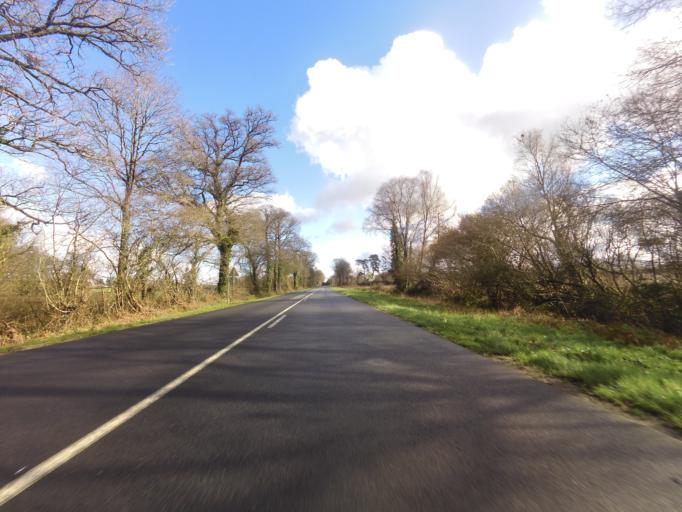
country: FR
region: Brittany
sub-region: Departement du Morbihan
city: Guemene-sur-Scorff
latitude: 48.0607
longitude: -3.1733
